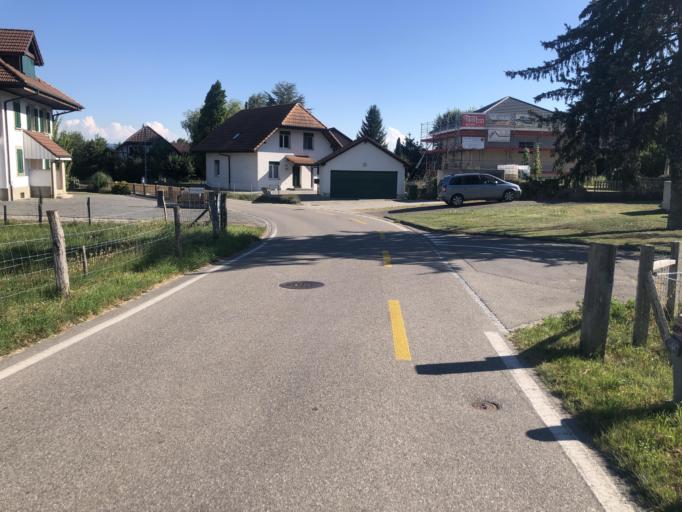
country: CH
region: Bern
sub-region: Bern-Mittelland District
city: Fraubrunnen
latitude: 47.0942
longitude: 7.5178
